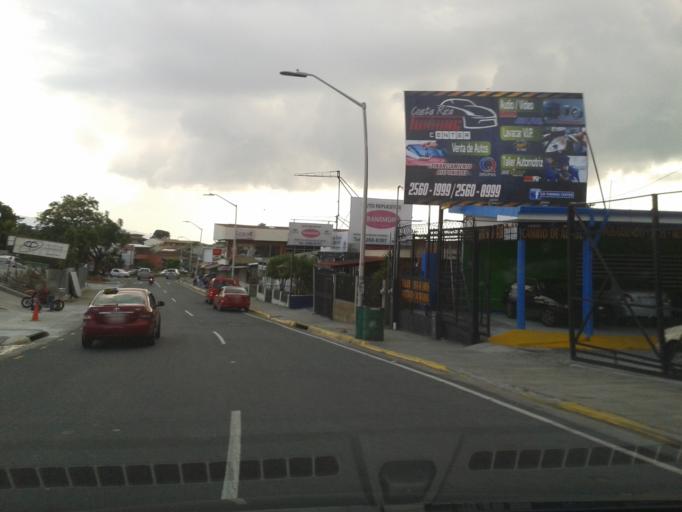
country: CR
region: Heredia
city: San Francisco
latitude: 9.9977
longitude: -84.1239
